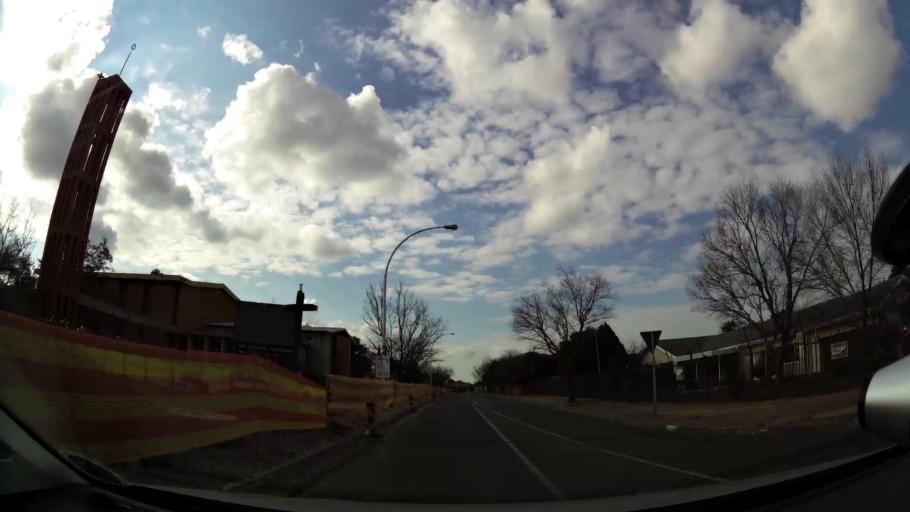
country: ZA
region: Orange Free State
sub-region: Mangaung Metropolitan Municipality
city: Bloemfontein
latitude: -29.0790
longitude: 26.2100
